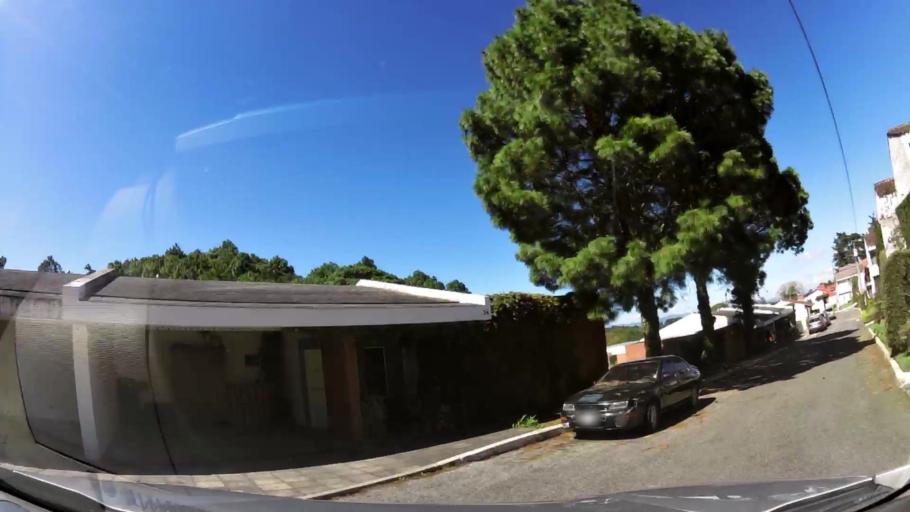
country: GT
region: Guatemala
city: San Jose Pinula
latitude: 14.5423
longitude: -90.4561
